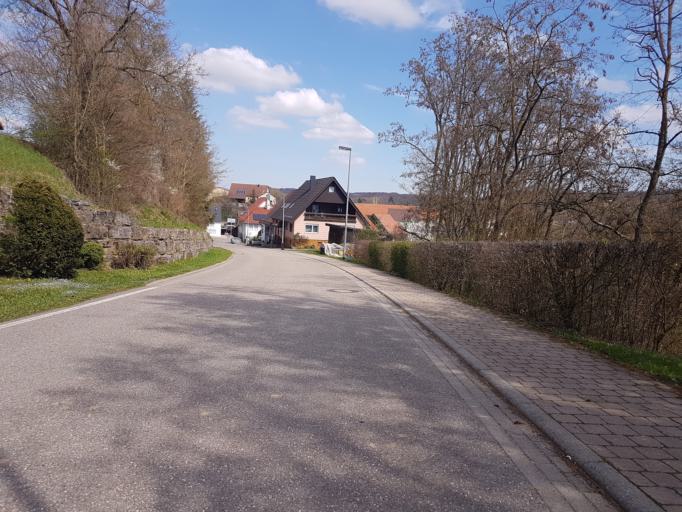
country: DE
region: Baden-Wuerttemberg
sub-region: Regierungsbezirk Stuttgart
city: Forchtenberg
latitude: 49.3703
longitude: 9.5385
